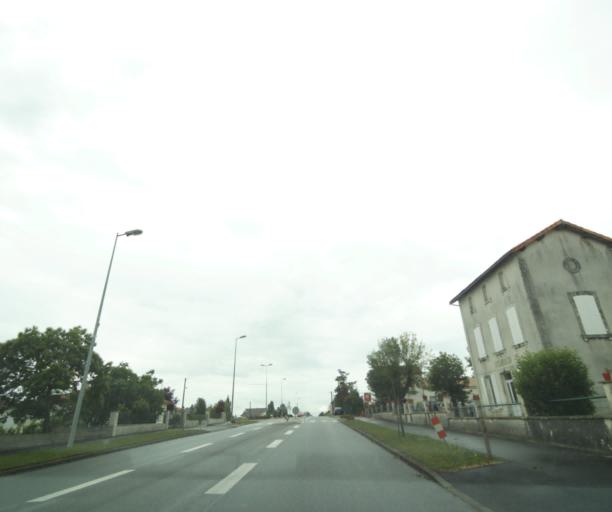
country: FR
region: Poitou-Charentes
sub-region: Departement des Deux-Sevres
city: Viennay
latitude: 46.6908
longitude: -0.2440
